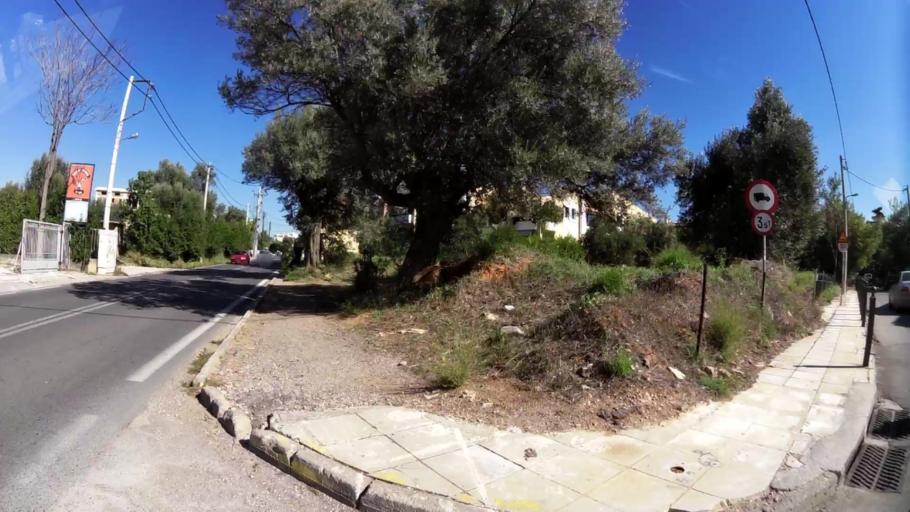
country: GR
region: Attica
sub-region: Nomarchia Athinas
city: Kifisia
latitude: 38.0837
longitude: 23.7979
